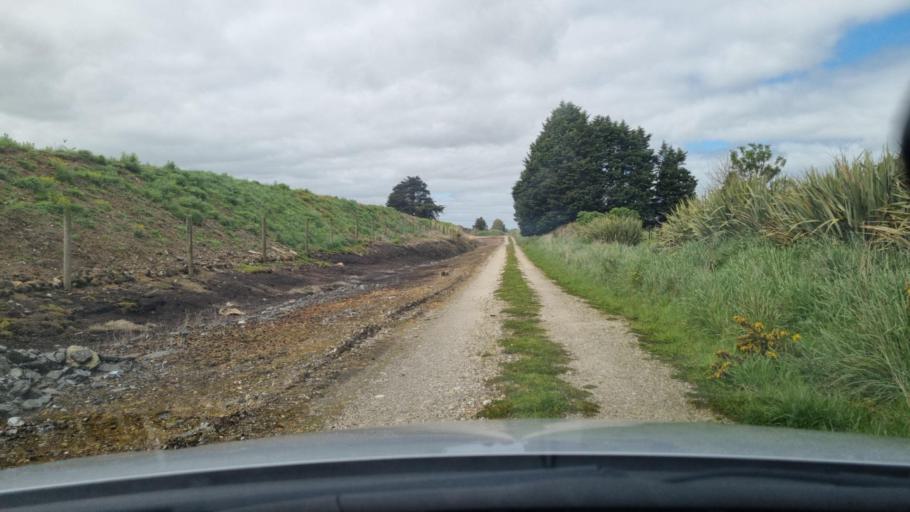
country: NZ
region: Southland
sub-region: Invercargill City
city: Invercargill
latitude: -46.3922
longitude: 168.4572
